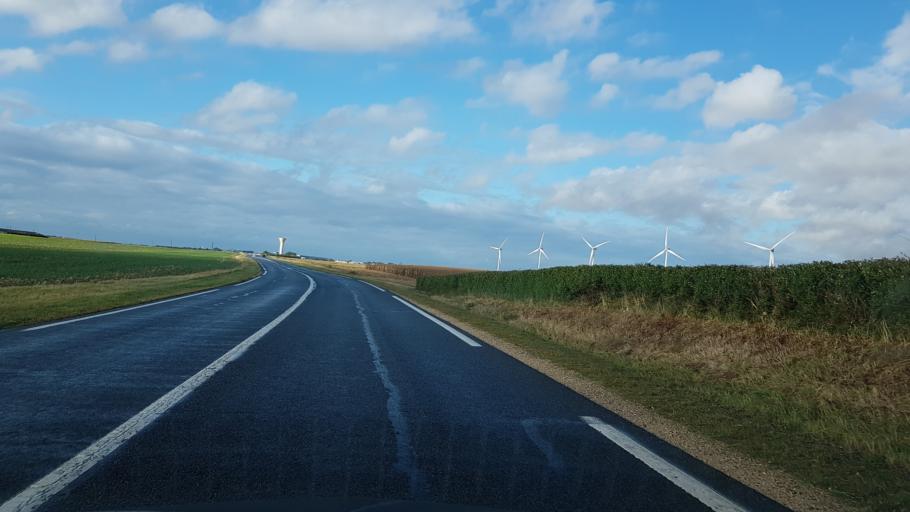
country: FR
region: Centre
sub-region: Departement du Loiret
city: Sermaises
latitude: 48.2659
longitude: 2.2118
